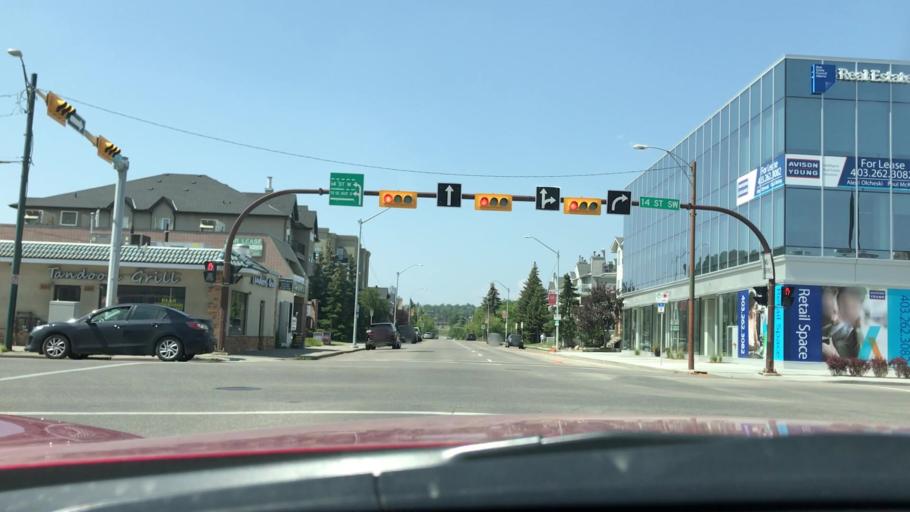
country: CA
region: Alberta
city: Calgary
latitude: 51.0433
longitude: -114.0945
